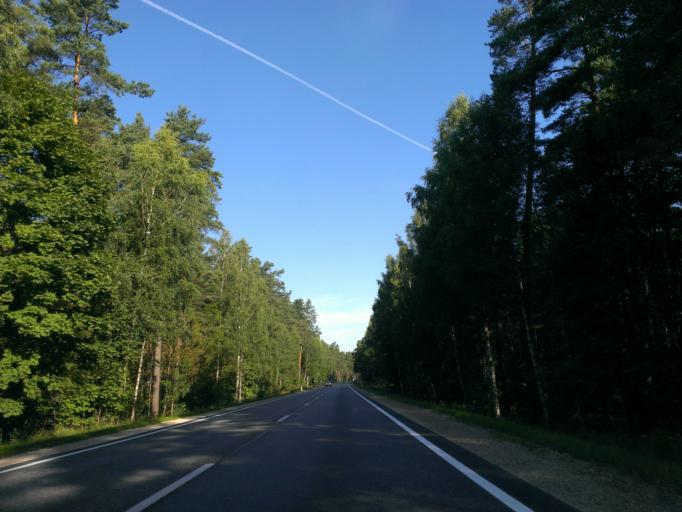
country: LV
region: Riga
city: Bergi
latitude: 56.9903
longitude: 24.3154
